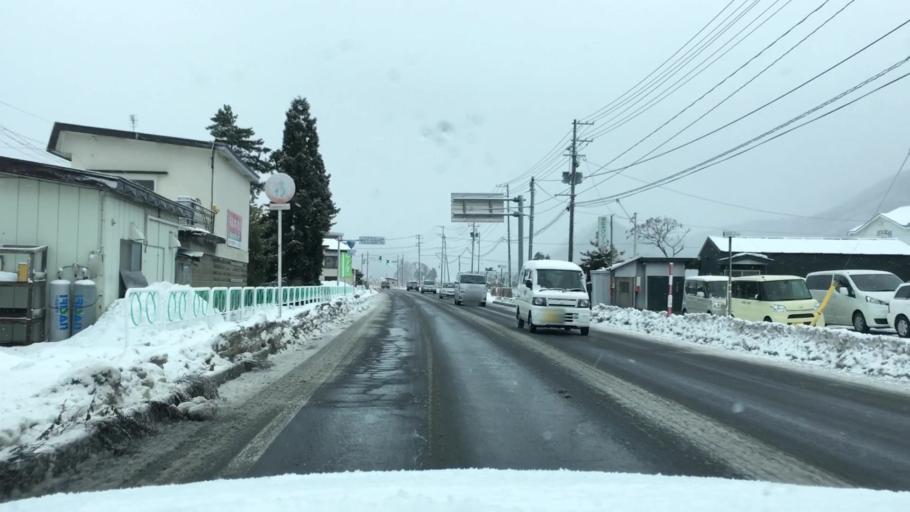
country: JP
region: Aomori
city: Hirosaki
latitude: 40.5450
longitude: 140.5524
